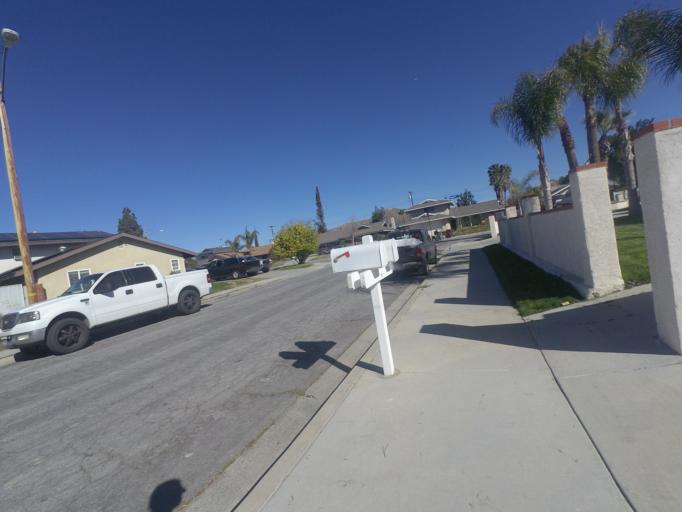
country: US
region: California
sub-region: Riverside County
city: March Air Force Base
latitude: 33.9226
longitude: -117.2682
